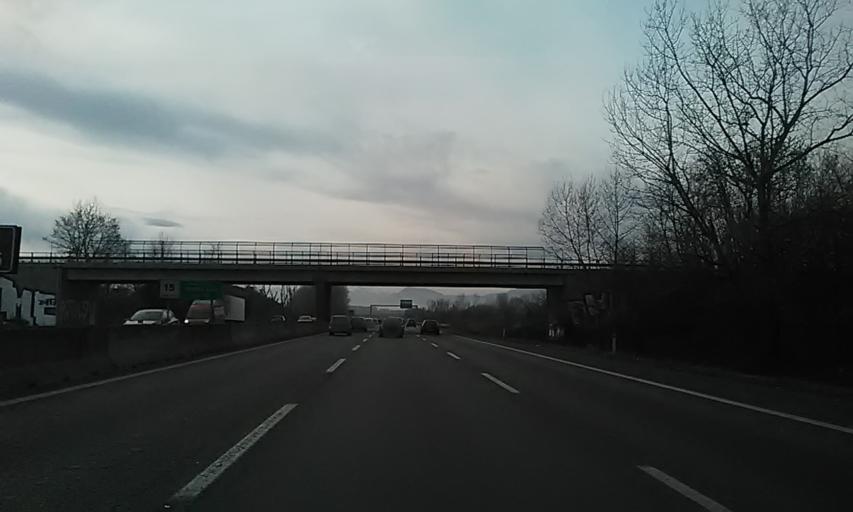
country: IT
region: Piedmont
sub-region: Provincia di Torino
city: Borgaro Torinese
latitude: 45.1278
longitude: 7.6736
